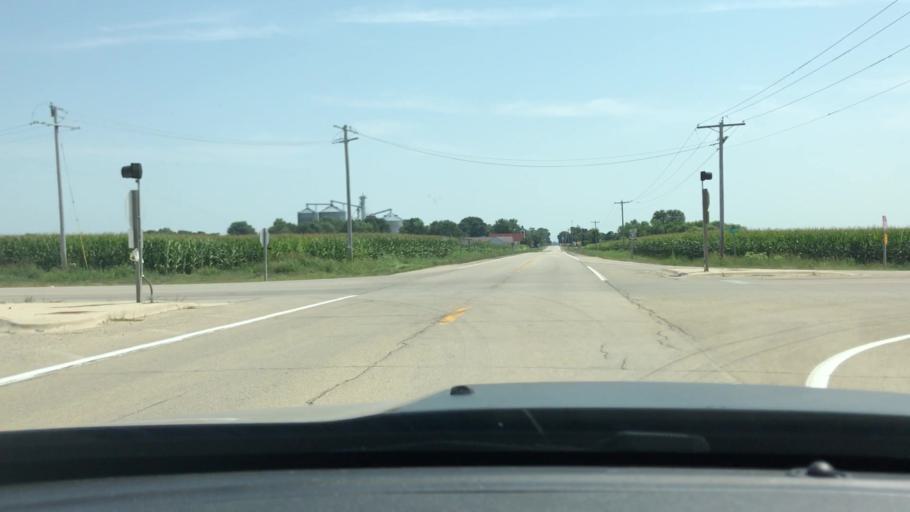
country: US
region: Illinois
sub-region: LaSalle County
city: Sheridan
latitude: 41.4851
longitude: -88.7415
